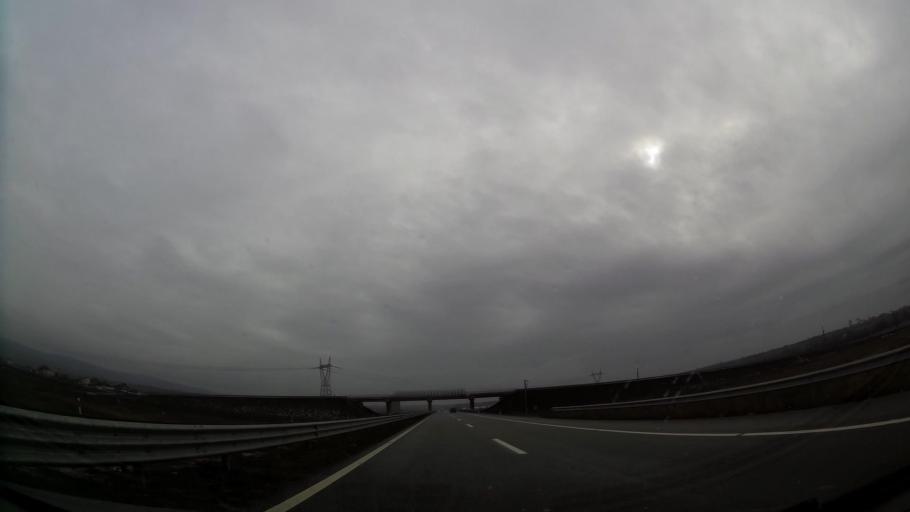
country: XK
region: Ferizaj
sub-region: Komuna e Ferizajt
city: Ferizaj
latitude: 42.4529
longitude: 21.1859
